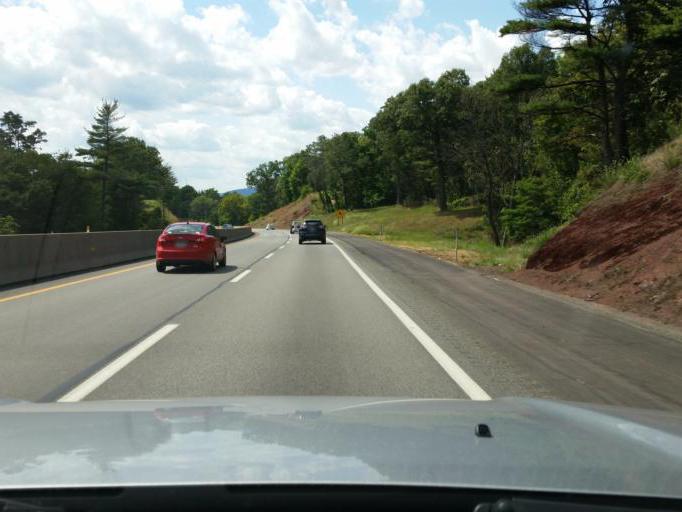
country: US
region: Pennsylvania
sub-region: Bedford County
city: Earlston
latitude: 39.9848
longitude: -78.2907
